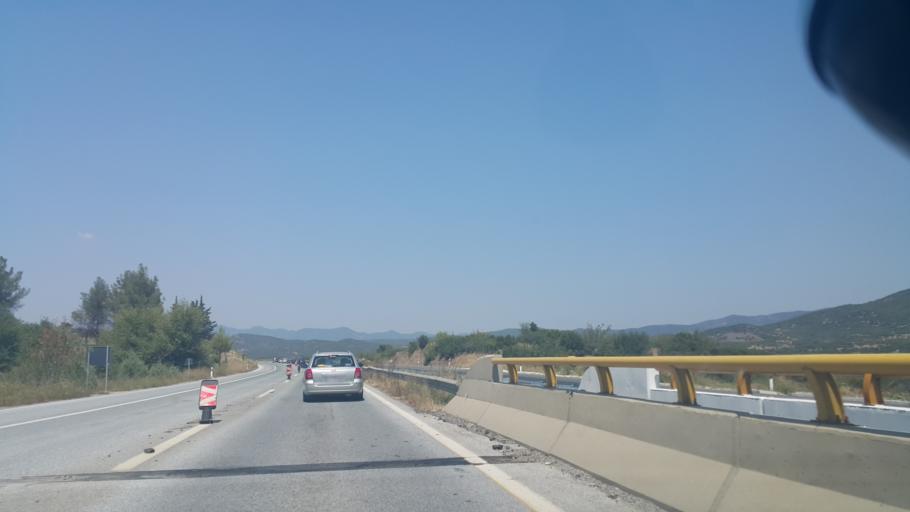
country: MK
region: Gevgelija
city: Gevgelija
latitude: 41.2277
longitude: 22.4914
